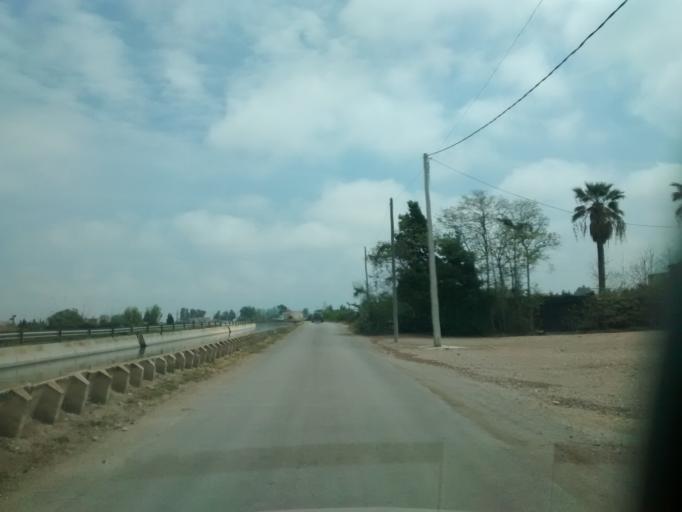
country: ES
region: Catalonia
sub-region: Provincia de Tarragona
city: Deltebre
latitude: 40.7024
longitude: 0.7253
